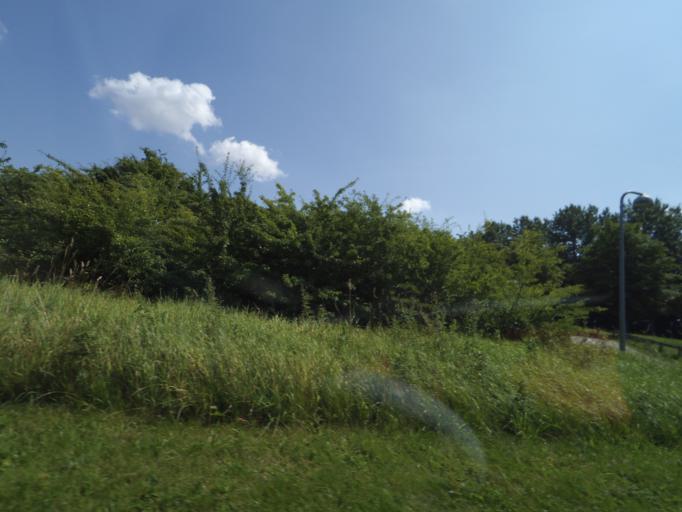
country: DK
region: South Denmark
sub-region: Odense Kommune
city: Neder Holluf
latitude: 55.3761
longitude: 10.4512
